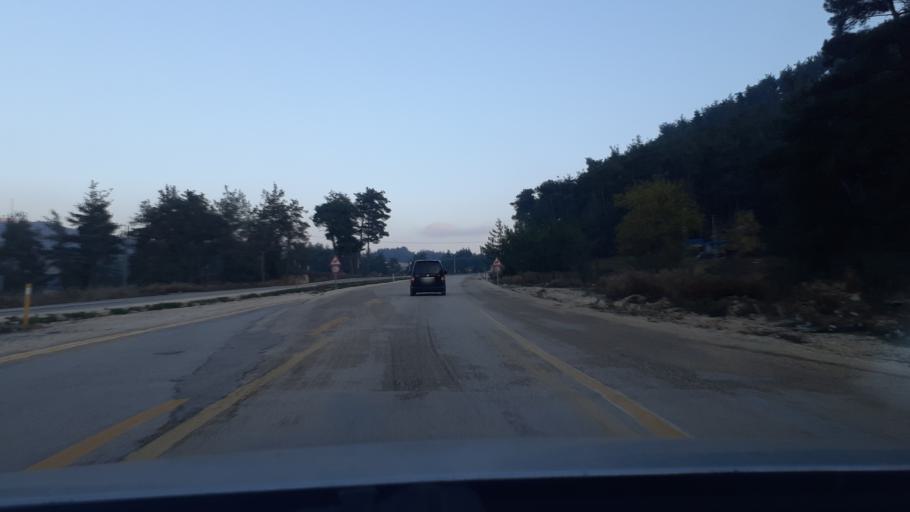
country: TR
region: Hatay
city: Yayladagi
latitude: 35.8955
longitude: 36.0791
